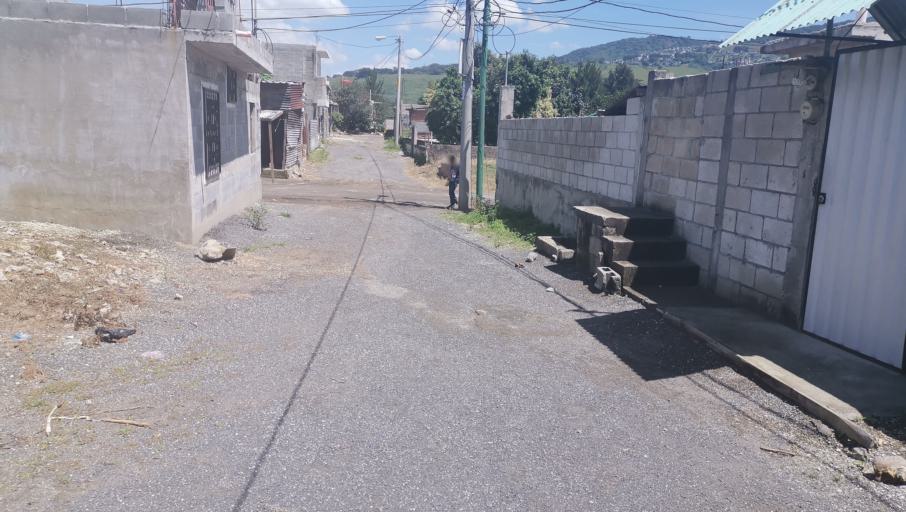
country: GT
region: Escuintla
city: San Vicente Pacaya
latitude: 14.4439
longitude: -90.6343
